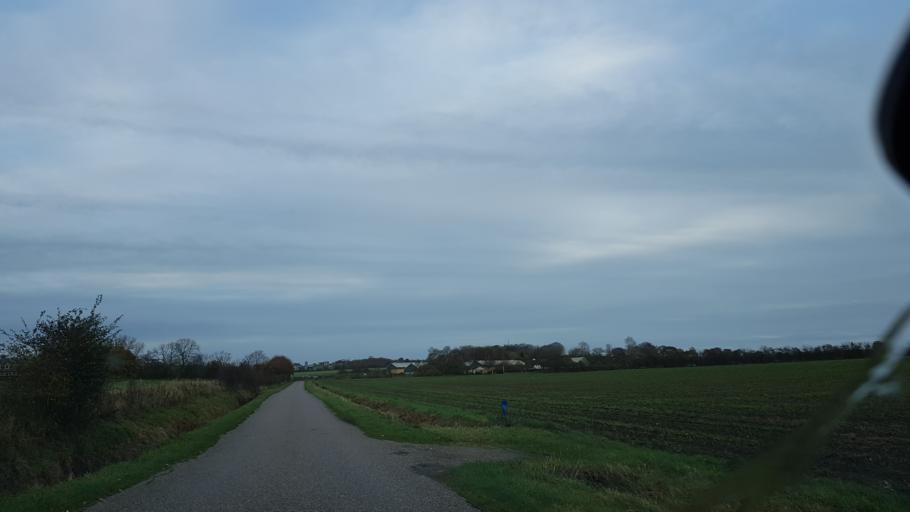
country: DK
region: South Denmark
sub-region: Haderslev Kommune
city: Vojens
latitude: 55.2484
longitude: 9.1837
